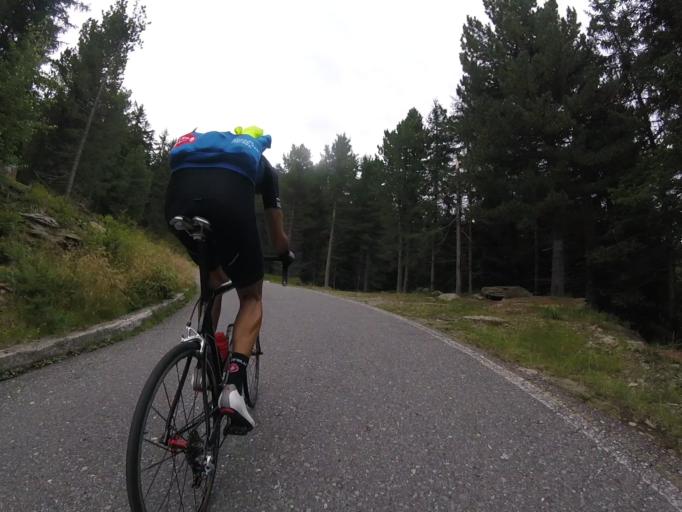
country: IT
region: Lombardy
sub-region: Provincia di Sondrio
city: Mazzo di Valtellina
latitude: 46.2465
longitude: 10.2886
